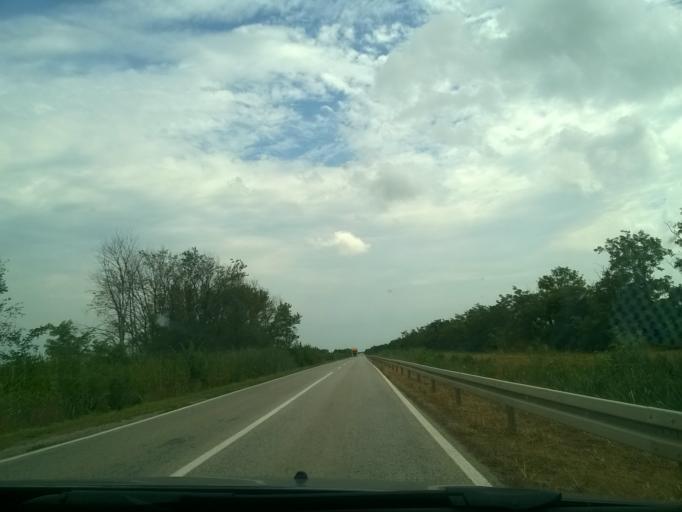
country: RS
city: Lazarevo
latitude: 45.3892
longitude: 20.5889
